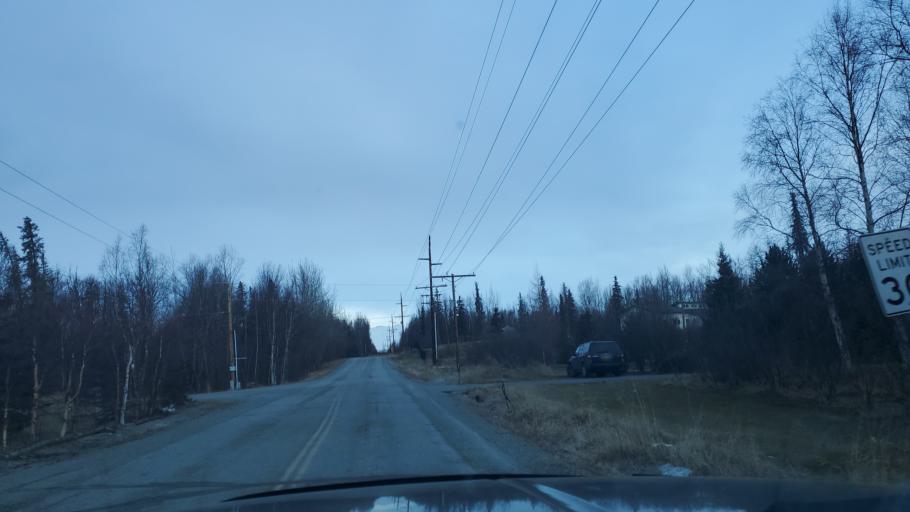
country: US
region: Alaska
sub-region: Matanuska-Susitna Borough
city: Lakes
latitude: 61.5719
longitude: -149.3297
